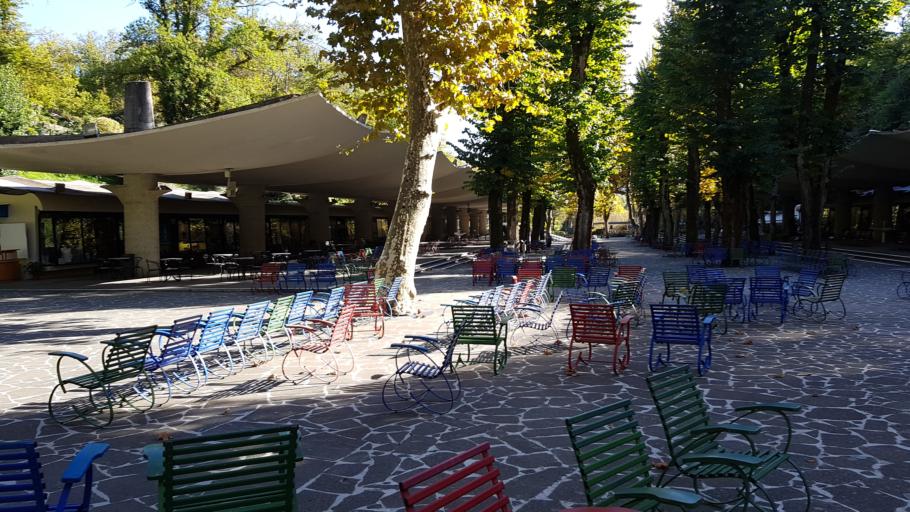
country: IT
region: Latium
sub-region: Provincia di Frosinone
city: Fiuggi
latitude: 41.7896
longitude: 13.2211
